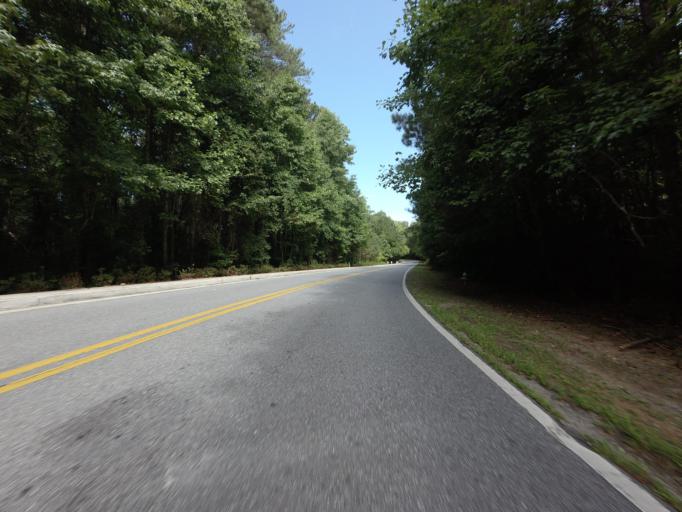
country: US
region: Georgia
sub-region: Fulton County
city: Johns Creek
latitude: 34.0623
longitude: -84.1779
